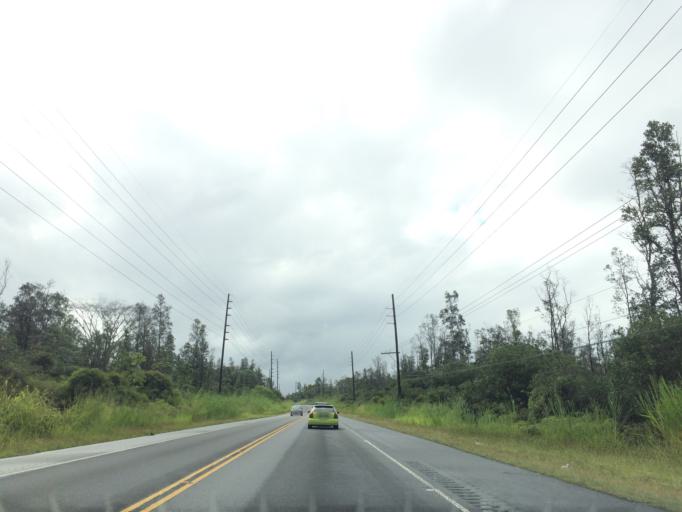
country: US
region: Hawaii
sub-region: Hawaii County
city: Ainaloa
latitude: 19.5255
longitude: -154.9699
